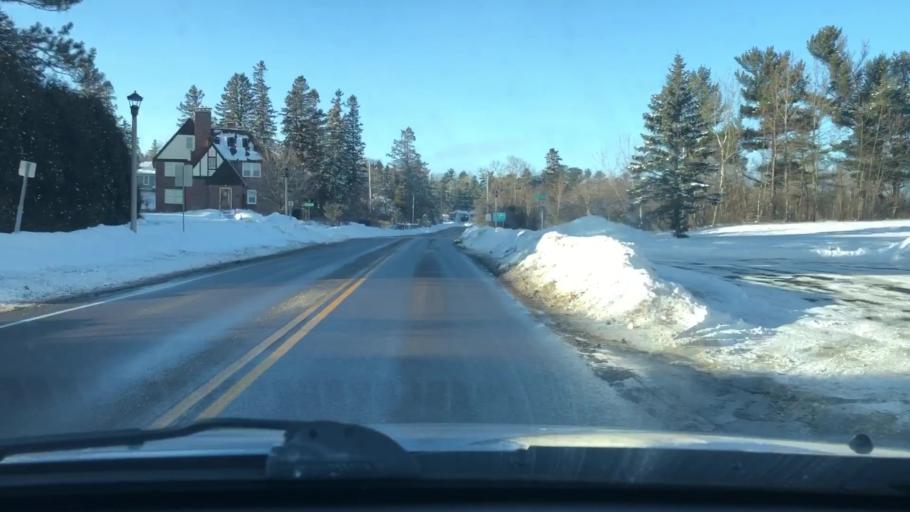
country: US
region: Minnesota
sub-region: Saint Louis County
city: Duluth
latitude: 46.8162
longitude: -92.0686
